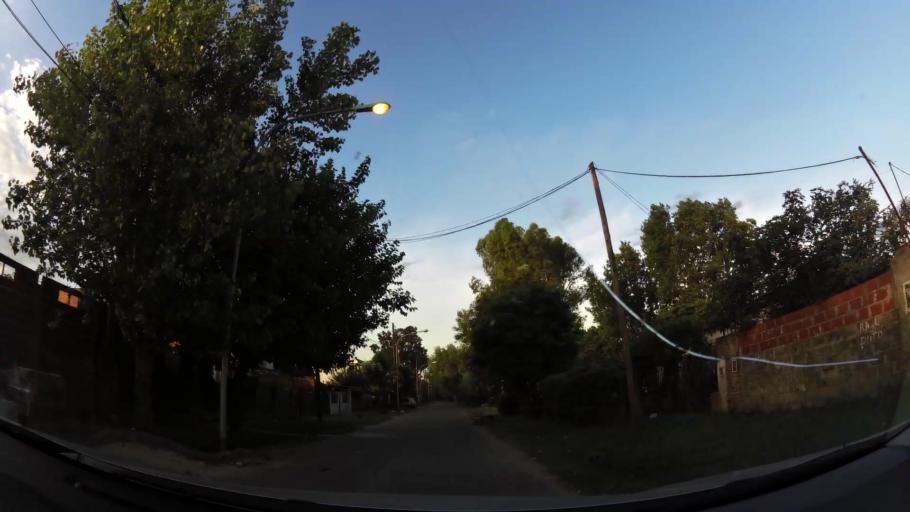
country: AR
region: Buenos Aires
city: Santa Catalina - Dique Lujan
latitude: -34.4447
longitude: -58.6610
